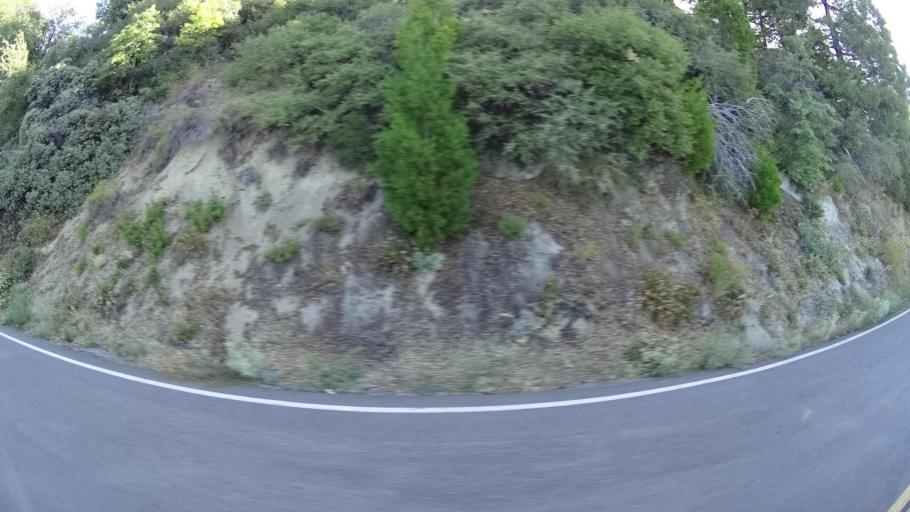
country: US
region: California
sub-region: Riverside County
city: Aguanga
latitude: 33.2973
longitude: -116.8402
